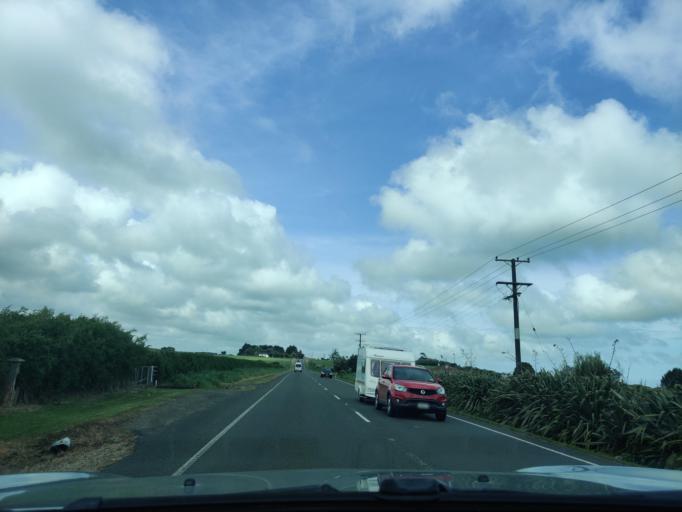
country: NZ
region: Manawatu-Wanganui
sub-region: Wanganui District
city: Wanganui
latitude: -39.8114
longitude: 174.7842
